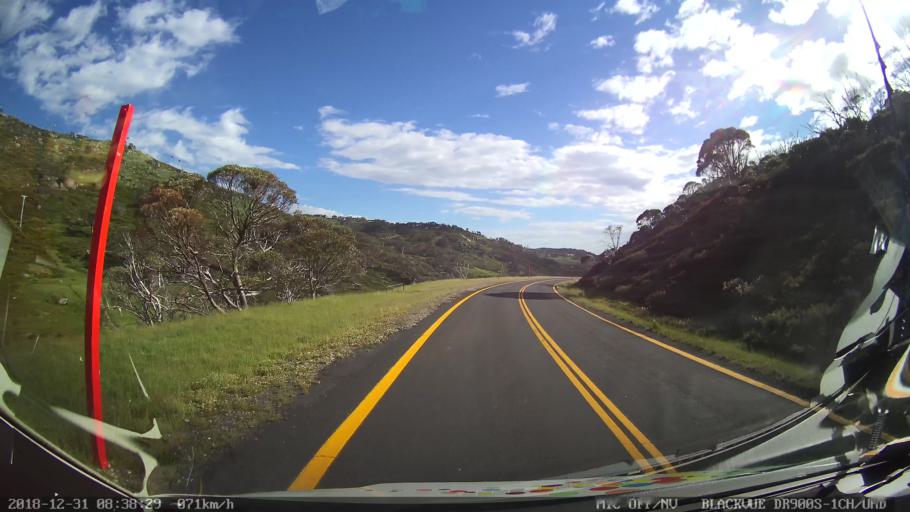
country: AU
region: New South Wales
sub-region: Snowy River
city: Jindabyne
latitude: -36.4142
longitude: 148.3958
